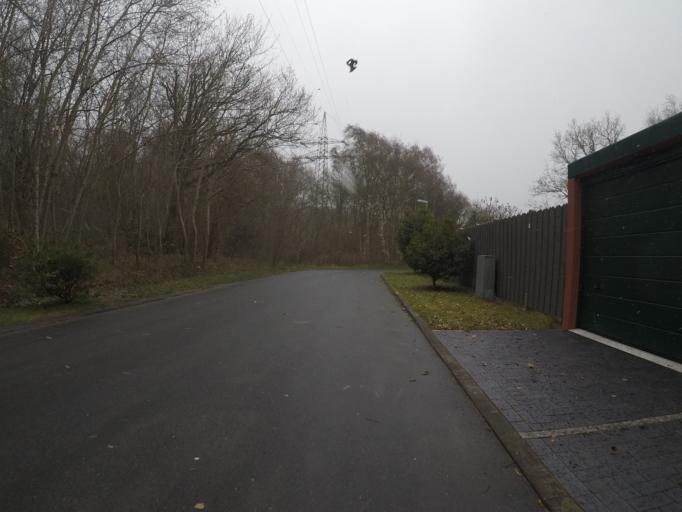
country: DE
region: Lower Saxony
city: Langen
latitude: 53.6128
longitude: 8.6289
